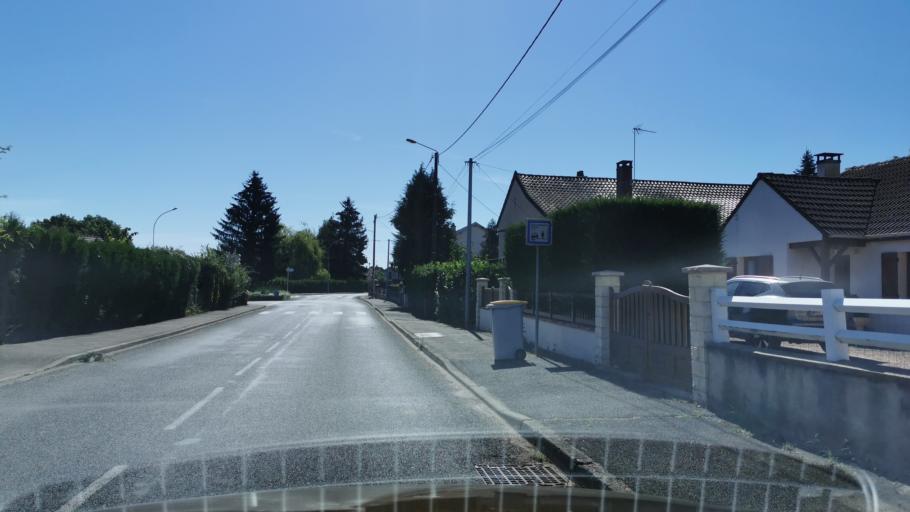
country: FR
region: Bourgogne
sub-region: Departement de Saone-et-Loire
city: Le Breuil
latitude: 46.8018
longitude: 4.4741
